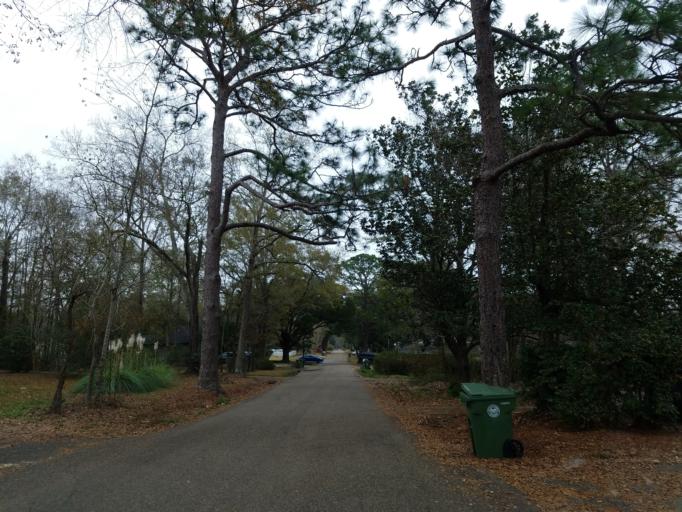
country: US
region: Mississippi
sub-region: Forrest County
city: Hattiesburg
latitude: 31.3210
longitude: -89.3275
